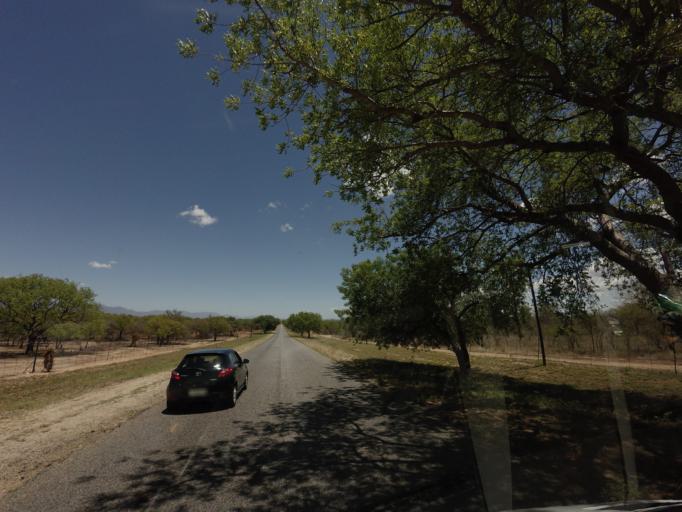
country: ZA
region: Limpopo
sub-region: Mopani District Municipality
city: Hoedspruit
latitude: -24.3918
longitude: 30.7545
